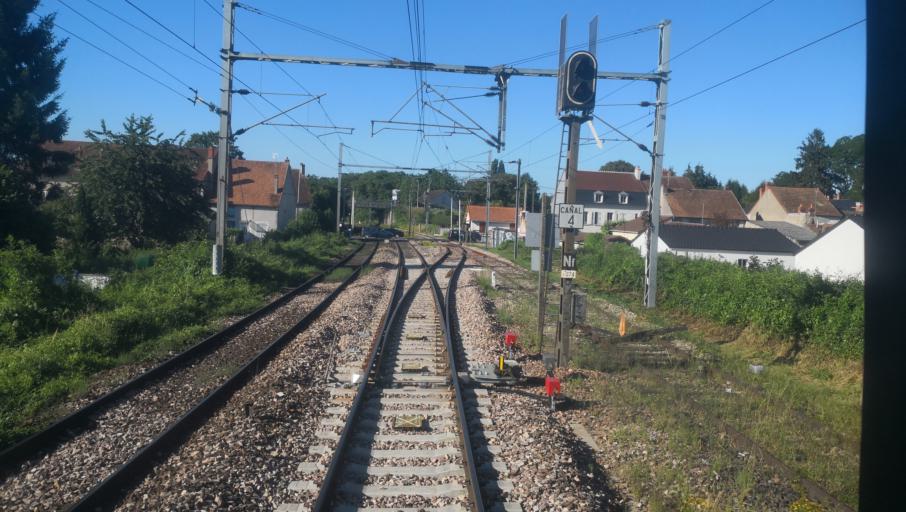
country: FR
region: Bourgogne
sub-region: Departement de la Nievre
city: Cosne-Cours-sur-Loire
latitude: 47.4109
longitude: 2.9318
